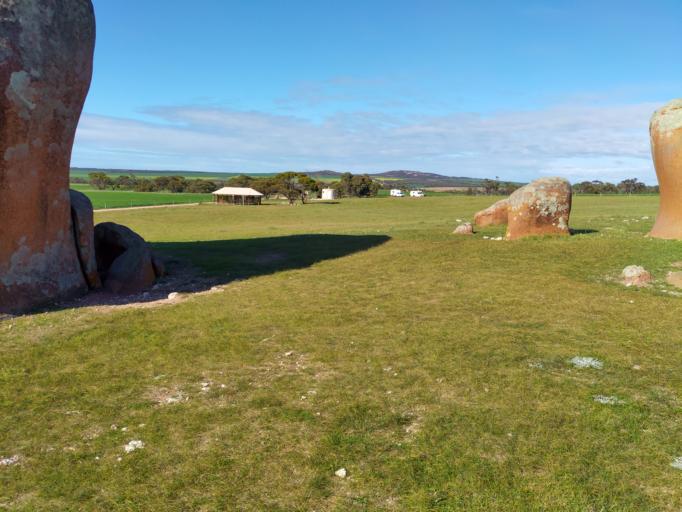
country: AU
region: South Australia
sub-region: Streaky Bay
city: Streaky Bay
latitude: -33.0152
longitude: 134.4913
